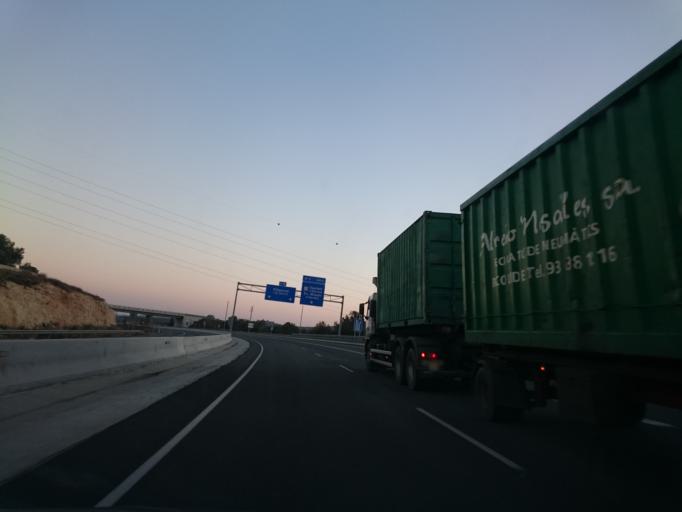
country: ES
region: Catalonia
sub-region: Provincia de Barcelona
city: Vilafranca del Penedes
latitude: 41.3268
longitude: 1.7117
